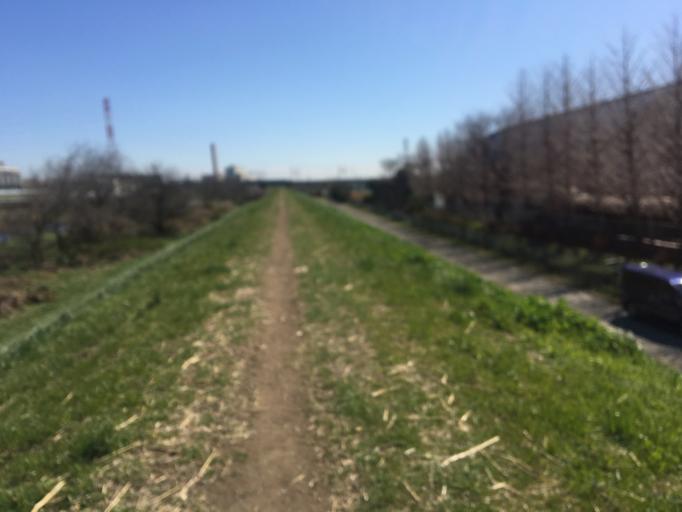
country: JP
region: Saitama
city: Shiki
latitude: 35.8255
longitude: 139.5973
